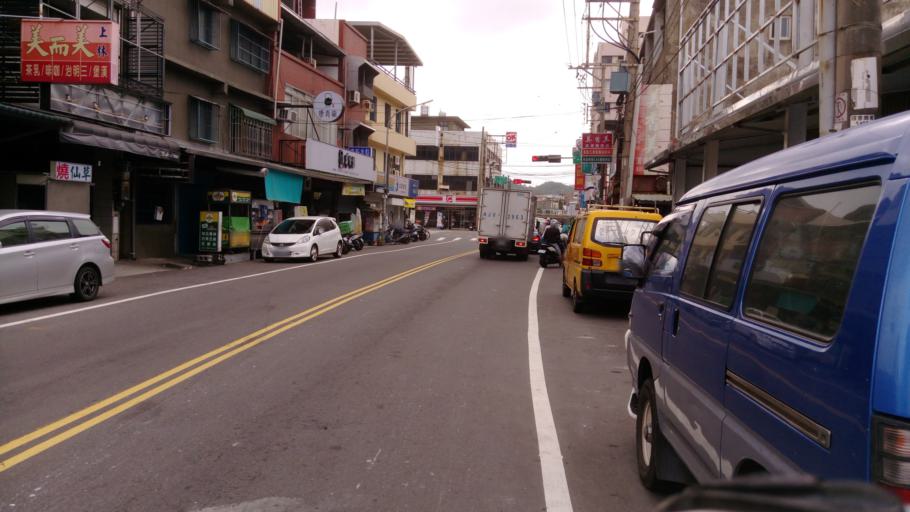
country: TW
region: Taiwan
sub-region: Hsinchu
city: Hsinchu
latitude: 24.7890
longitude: 120.9283
